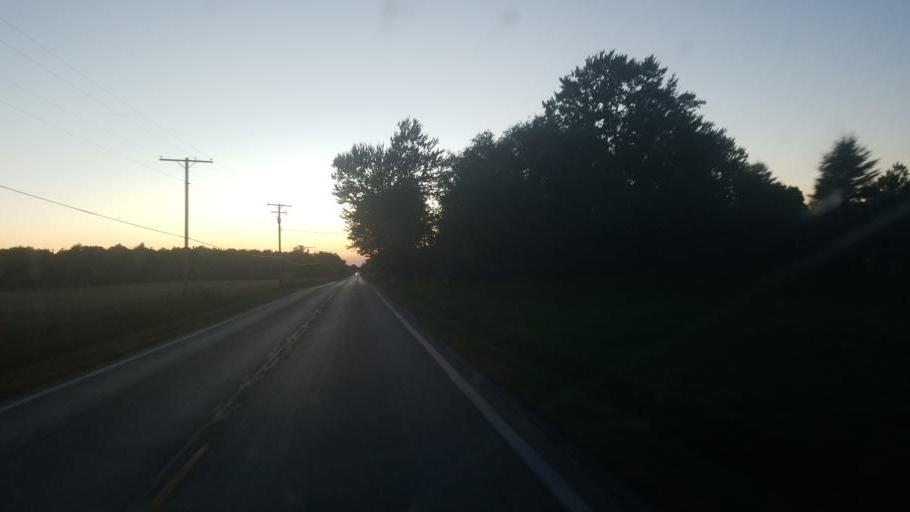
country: US
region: Ohio
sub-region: Ashtabula County
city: Jefferson
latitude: 41.7514
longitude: -80.6890
